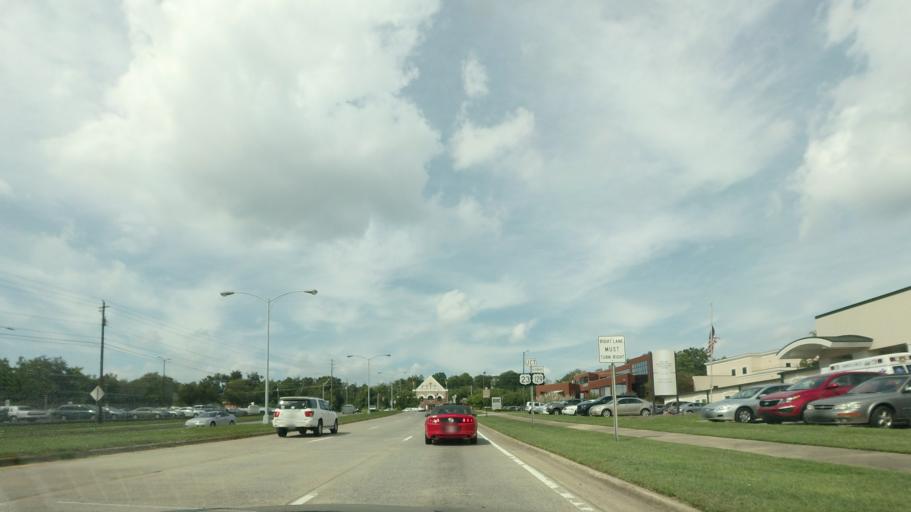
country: US
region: Georgia
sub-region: Bibb County
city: Macon
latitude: 32.8468
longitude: -83.6167
